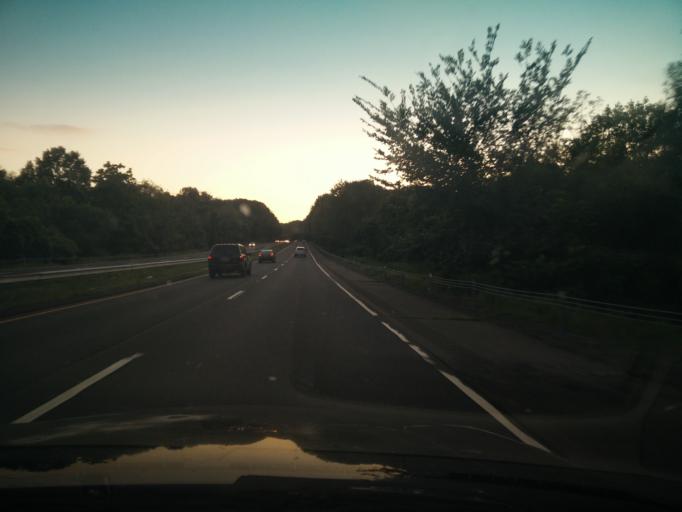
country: US
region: Connecticut
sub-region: New Haven County
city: New Haven
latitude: 41.3549
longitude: -72.9519
